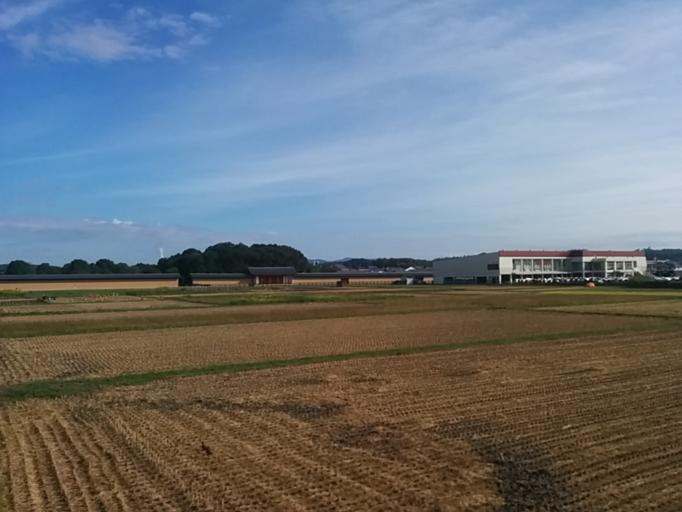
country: JP
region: Nara
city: Nara-shi
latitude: 34.6871
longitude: 135.8002
